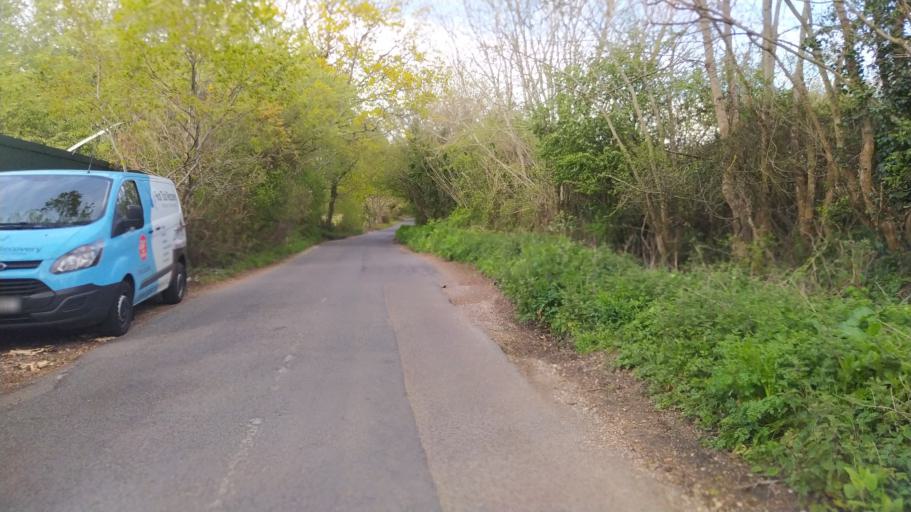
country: GB
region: England
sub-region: Hampshire
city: Bursledon
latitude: 50.8961
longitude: -1.3337
